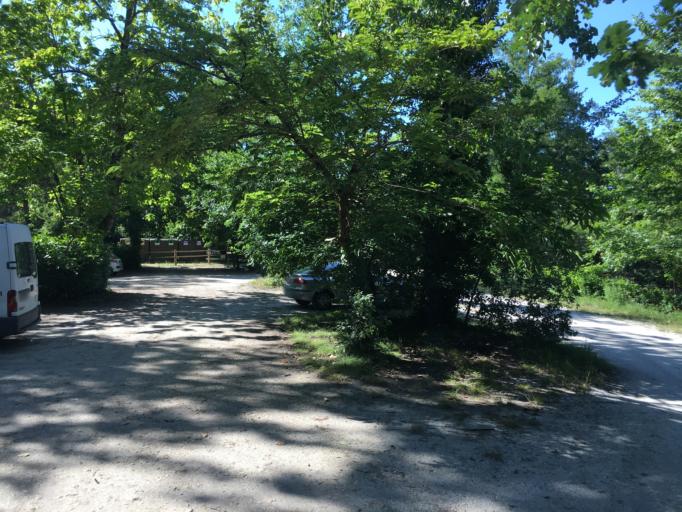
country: FR
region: Aquitaine
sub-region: Departement de la Gironde
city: Belin-Beliet
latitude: 44.4973
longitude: -0.6482
